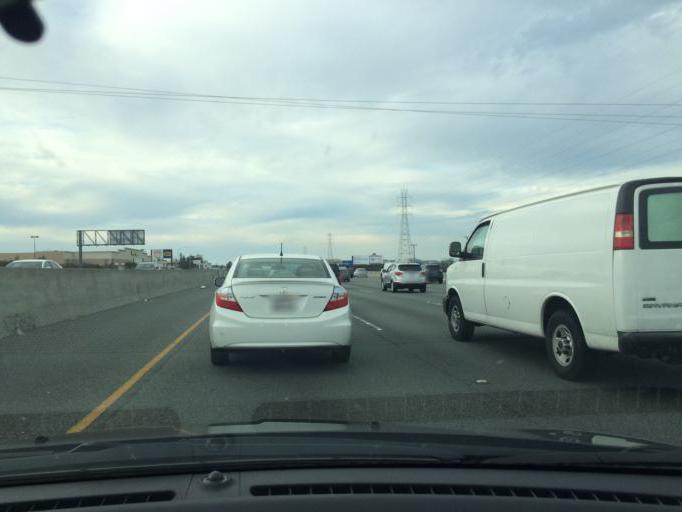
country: US
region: California
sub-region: San Mateo County
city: Redwood City
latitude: 37.5012
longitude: -122.2416
